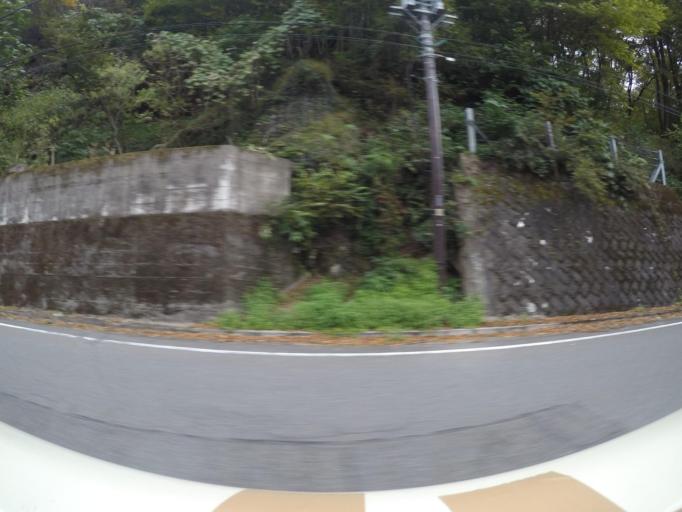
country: JP
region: Gunma
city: Tomioka
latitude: 36.0838
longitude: 138.7210
